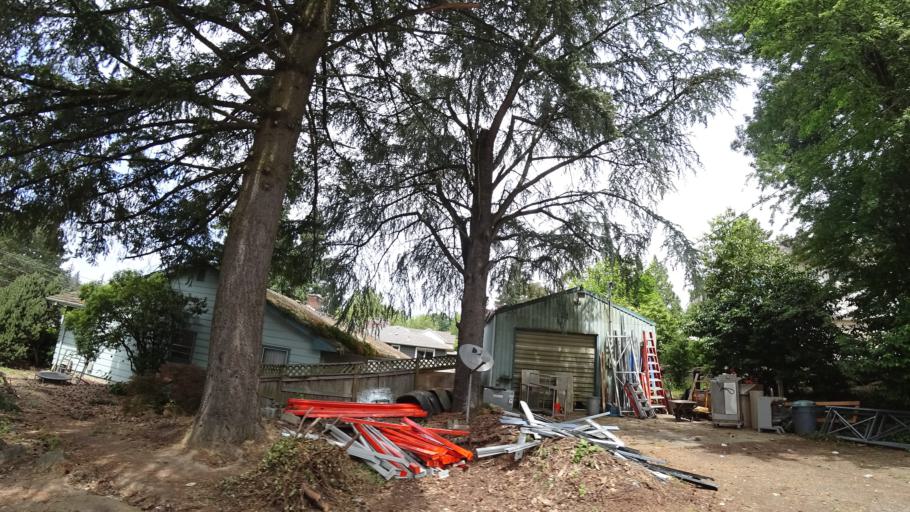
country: US
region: Oregon
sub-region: Washington County
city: Metzger
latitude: 45.4466
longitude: -122.7586
